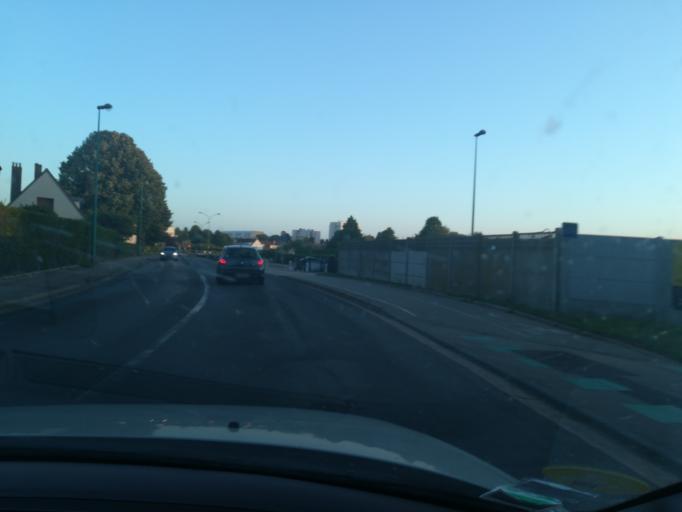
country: FR
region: Haute-Normandie
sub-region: Departement de la Seine-Maritime
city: Bois-Guillaume
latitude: 49.4649
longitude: 1.1296
